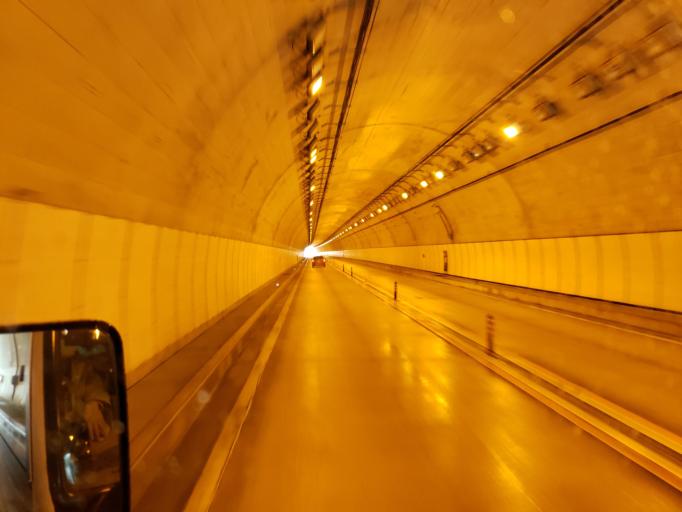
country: JP
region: Hyogo
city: Toyooka
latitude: 35.2387
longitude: 134.7853
